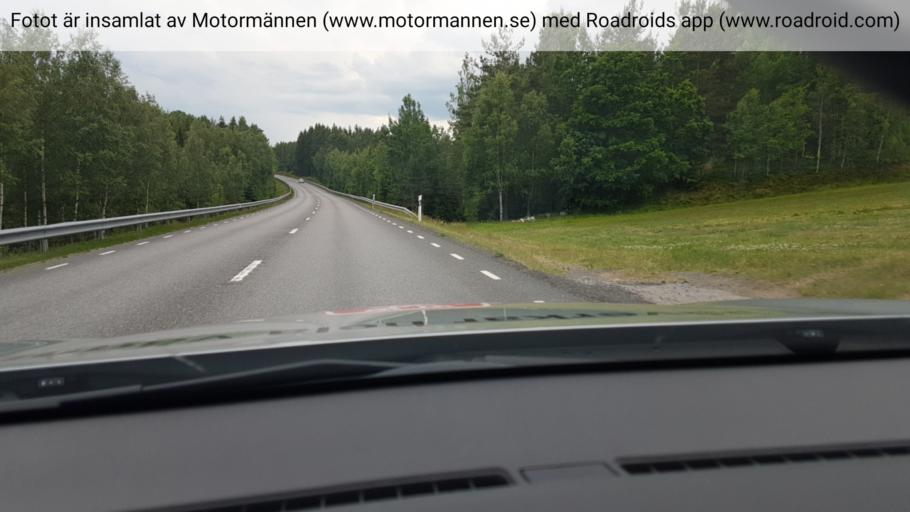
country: SE
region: Joenkoeping
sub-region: Habo Kommun
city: Habo
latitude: 57.9826
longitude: 14.1072
